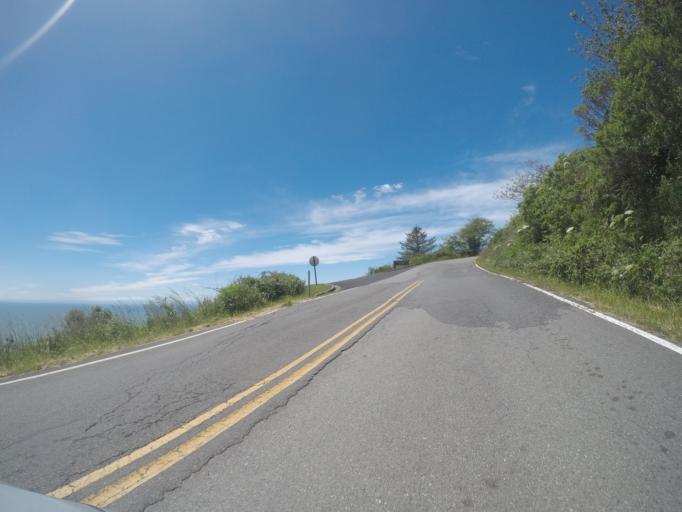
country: US
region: California
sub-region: Del Norte County
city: Bertsch-Oceanview
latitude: 41.5544
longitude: -124.0855
